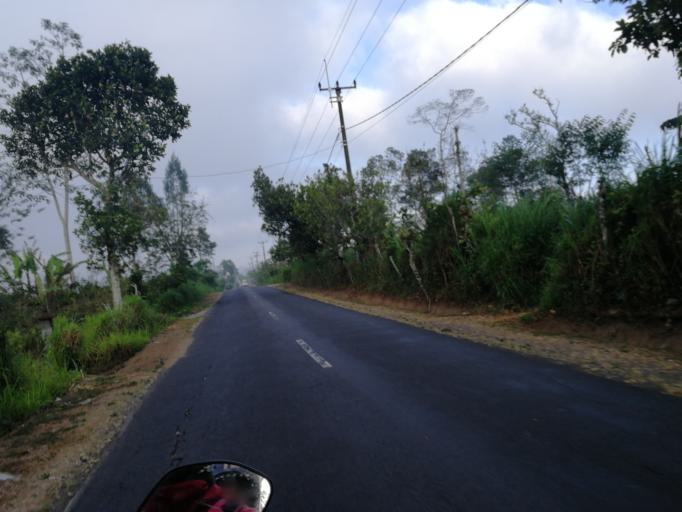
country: ID
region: Bali
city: Banjar Kedisan
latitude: -8.2239
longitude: 115.2538
